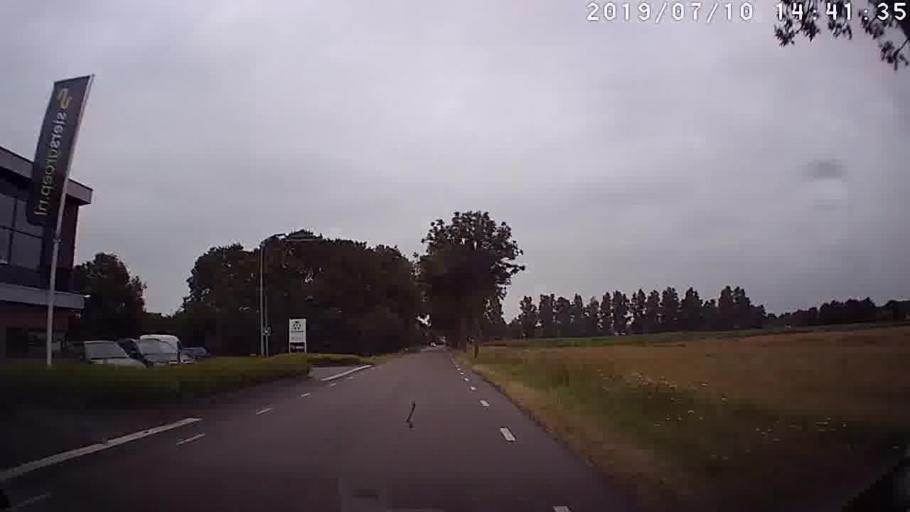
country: NL
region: Gelderland
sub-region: Gemeente Hattem
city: Hattem
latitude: 52.4858
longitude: 6.0383
